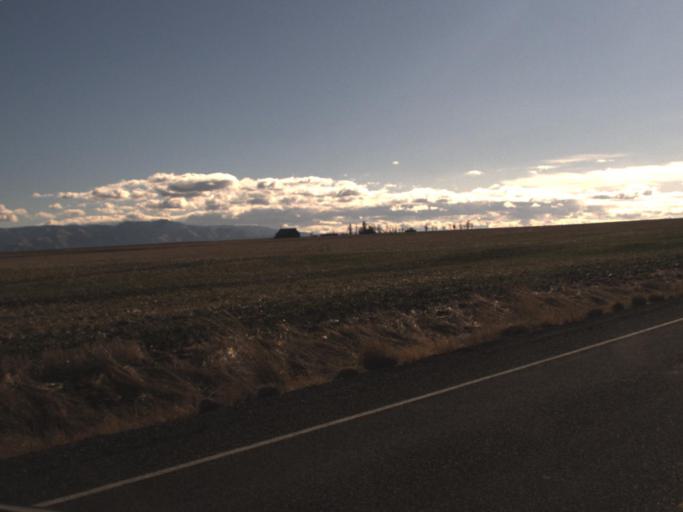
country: US
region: Washington
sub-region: Asotin County
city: Asotin
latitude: 46.2169
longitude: -117.0703
